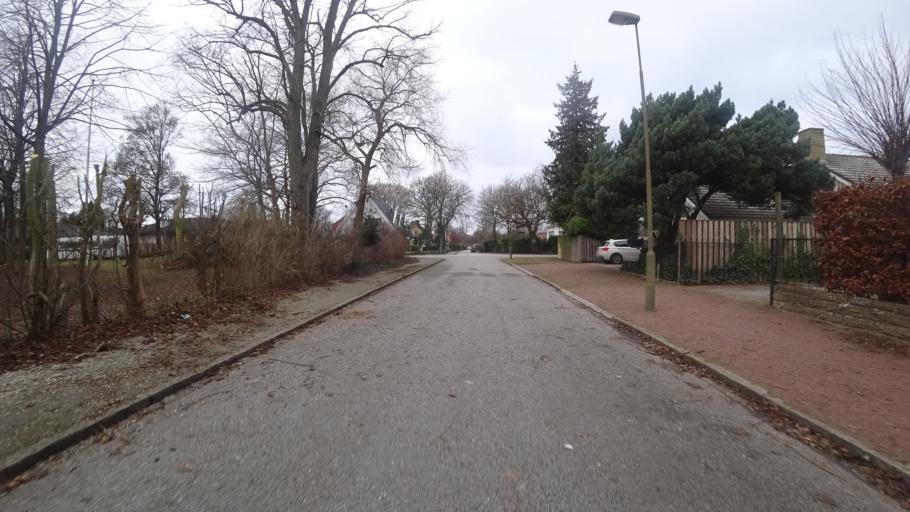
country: SE
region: Skane
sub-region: Malmo
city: Malmoe
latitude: 55.5893
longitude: 12.9569
